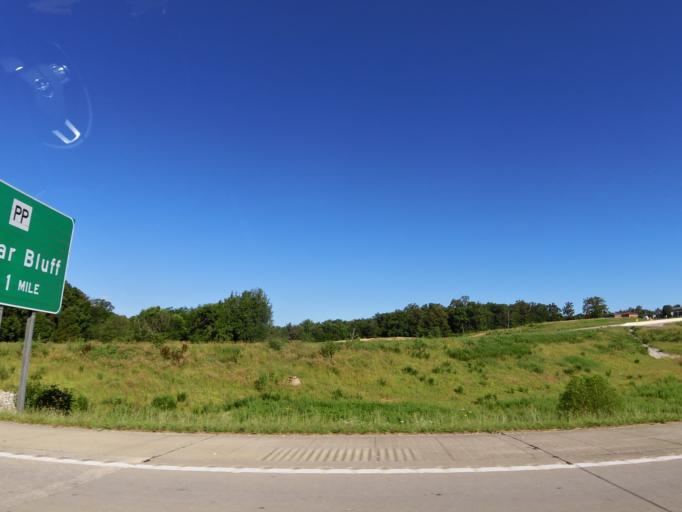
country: US
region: Missouri
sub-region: Butler County
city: Poplar Bluff
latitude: 36.7867
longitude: -90.4509
